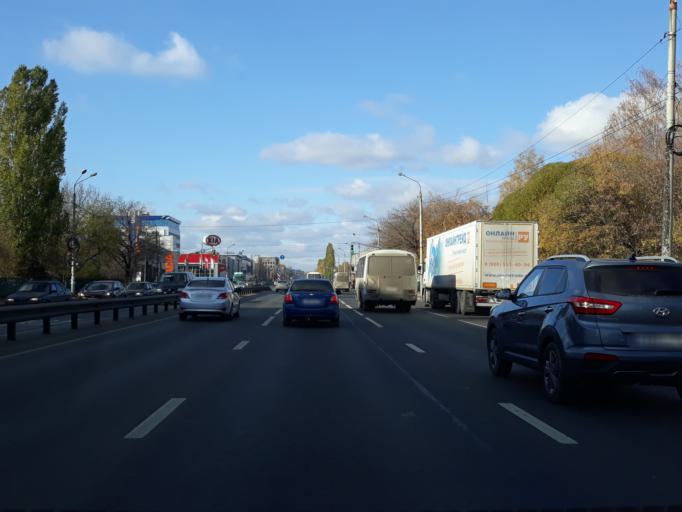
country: RU
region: Nizjnij Novgorod
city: Nizhniy Novgorod
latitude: 56.2592
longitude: 43.9311
